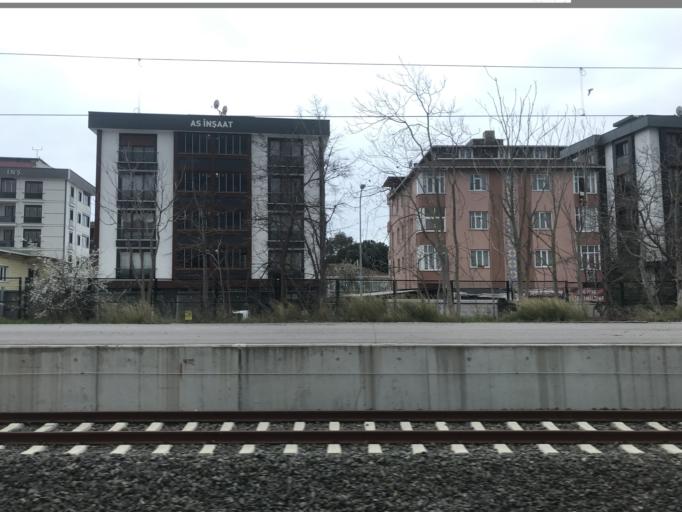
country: TR
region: Istanbul
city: Icmeler
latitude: 40.8284
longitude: 29.3242
